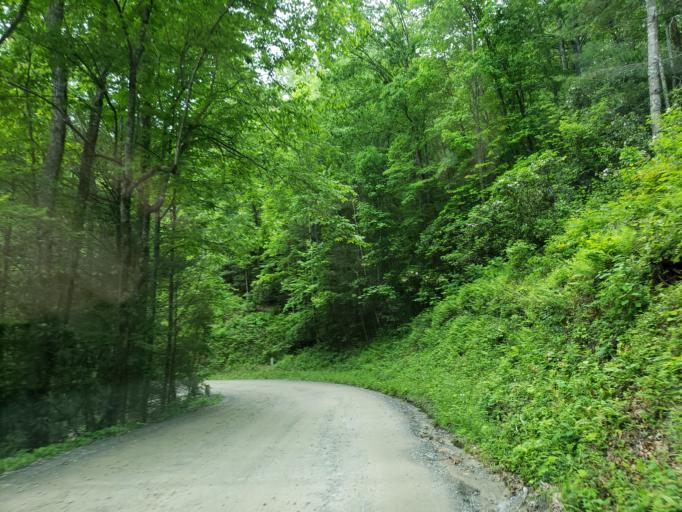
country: US
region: Georgia
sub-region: Fannin County
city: Blue Ridge
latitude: 34.8566
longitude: -84.4221
